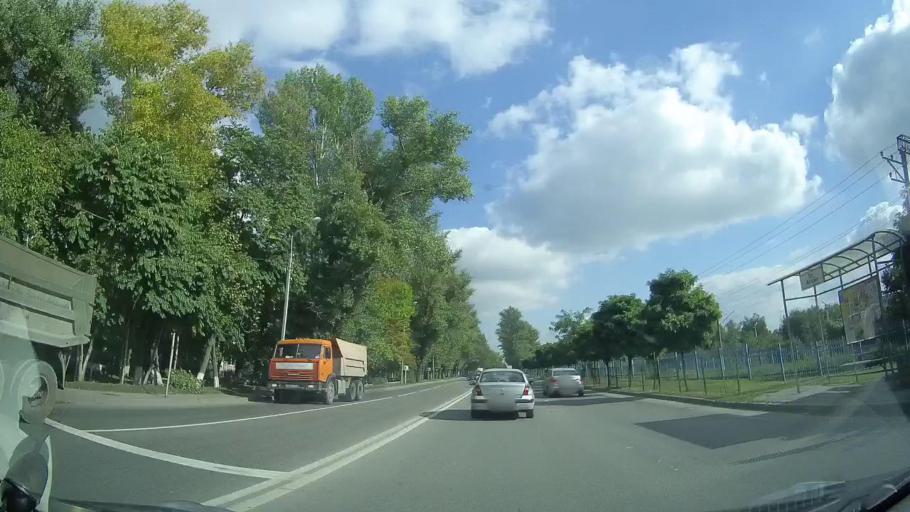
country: RU
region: Rostov
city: Imeni Chkalova
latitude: 47.2627
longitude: 39.7785
